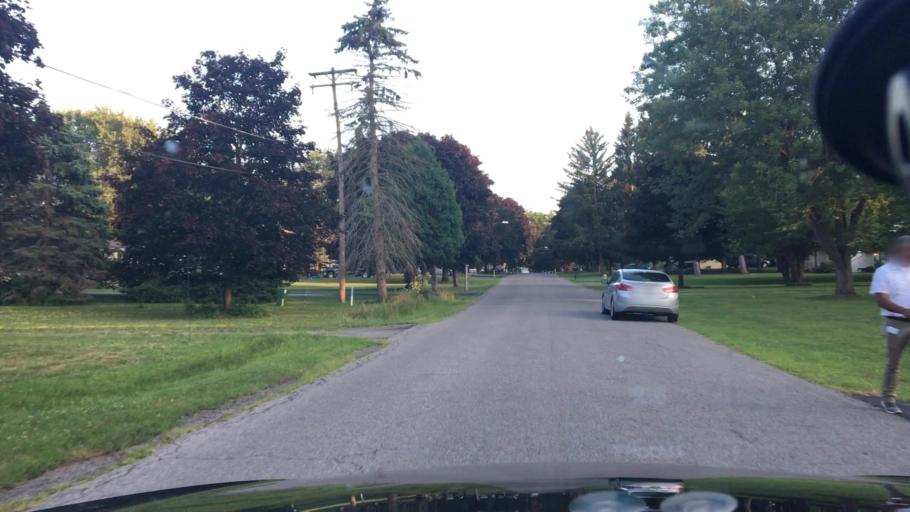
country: US
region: New York
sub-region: Erie County
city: Orchard Park
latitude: 42.7887
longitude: -78.7409
